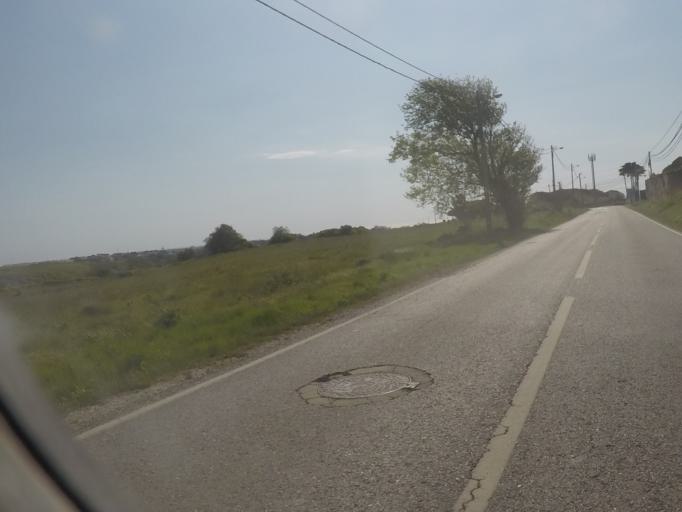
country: PT
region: Setubal
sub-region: Sesimbra
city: Sesimbra
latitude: 38.4463
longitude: -9.1570
